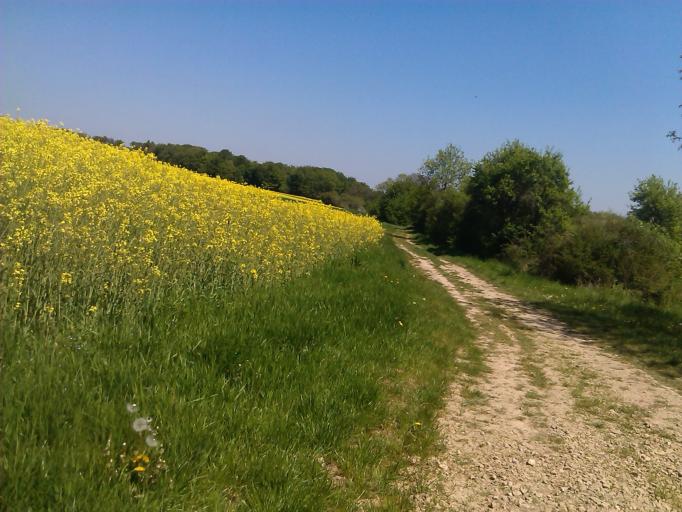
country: DE
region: Baden-Wuerttemberg
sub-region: Regierungsbezirk Stuttgart
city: Zaberfeld
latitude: 49.0476
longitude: 8.9309
